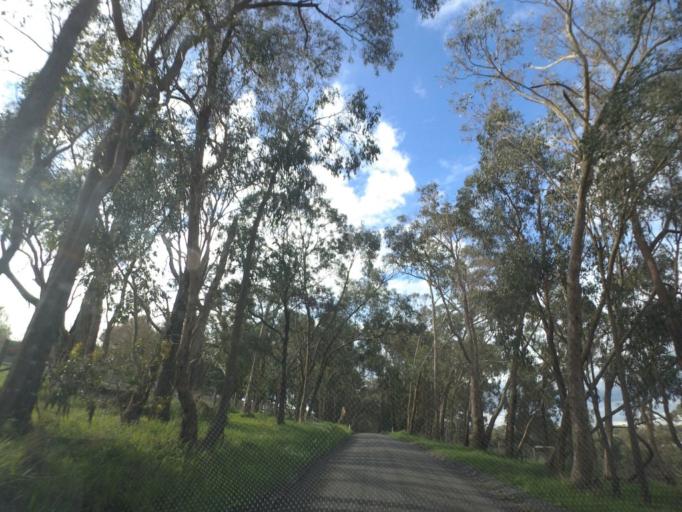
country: AU
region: Victoria
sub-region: Yarra Ranges
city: Mount Evelyn
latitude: -37.7615
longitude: 145.4091
